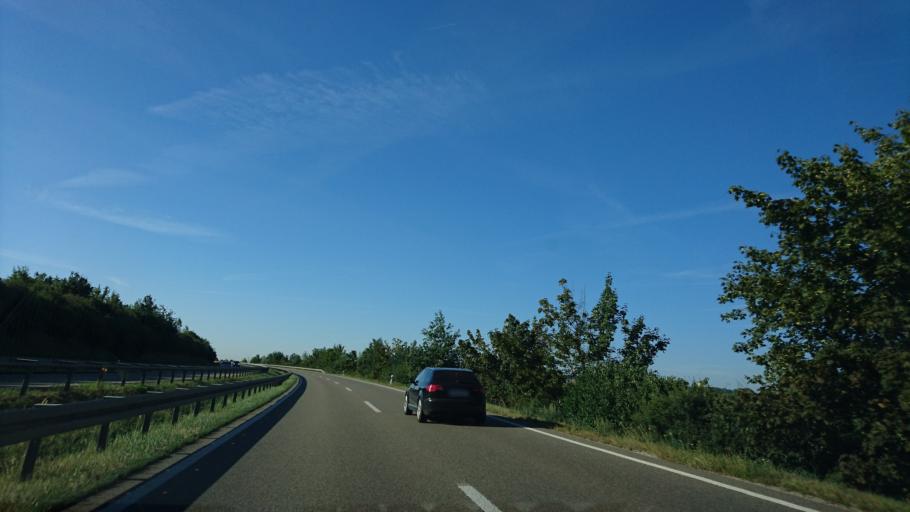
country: DE
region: Bavaria
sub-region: Swabia
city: Biberbach
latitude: 48.5299
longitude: 10.8310
